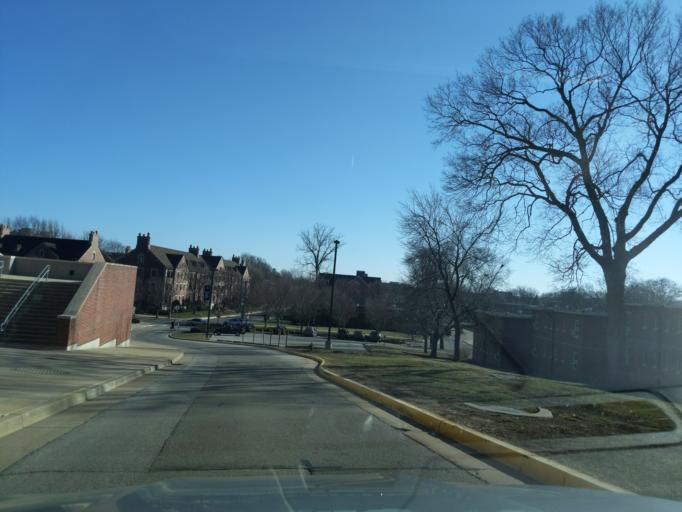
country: US
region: Indiana
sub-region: Tippecanoe County
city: West Lafayette
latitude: 40.4339
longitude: -86.9196
